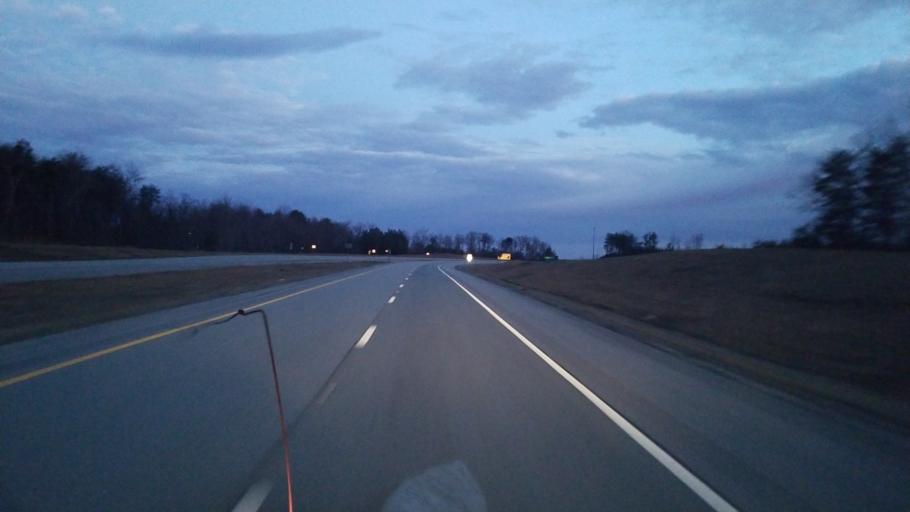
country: US
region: Tennessee
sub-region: Van Buren County
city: Spencer
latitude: 35.6206
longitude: -85.4757
